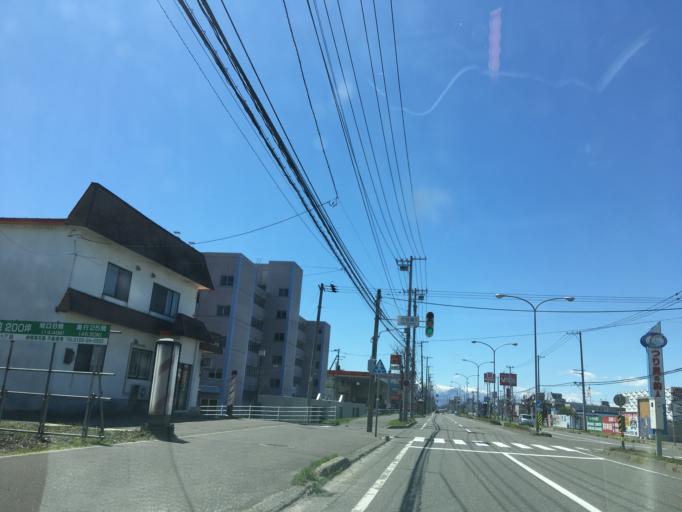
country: JP
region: Hokkaido
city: Obihiro
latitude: 42.9303
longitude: 143.1807
